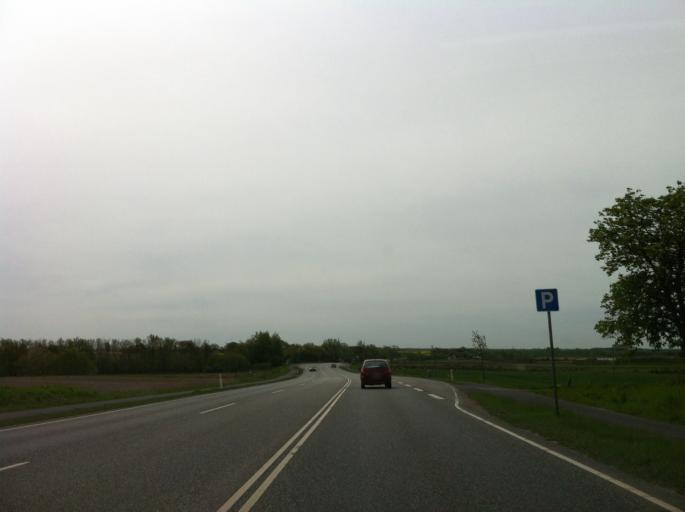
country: DK
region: Zealand
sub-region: Roskilde Kommune
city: Gundsomagle
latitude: 55.7395
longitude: 12.1281
